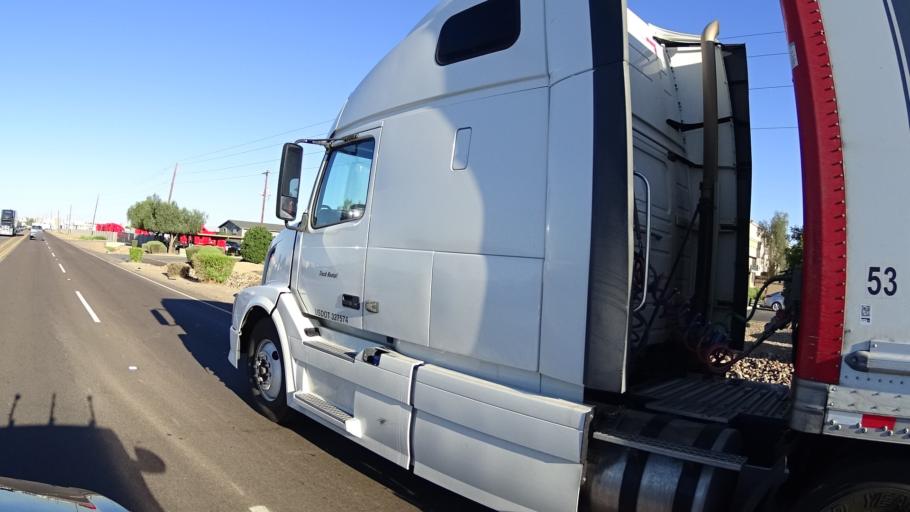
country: US
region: Arizona
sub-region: Maricopa County
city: Tolleson
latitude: 33.4371
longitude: -112.2340
